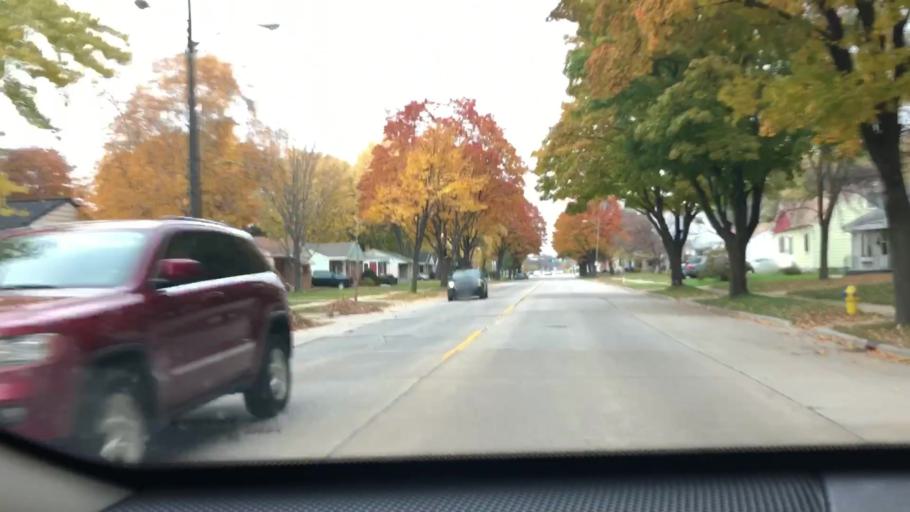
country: US
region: Wisconsin
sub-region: Brown County
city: Green Bay
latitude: 44.5148
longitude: -88.0480
